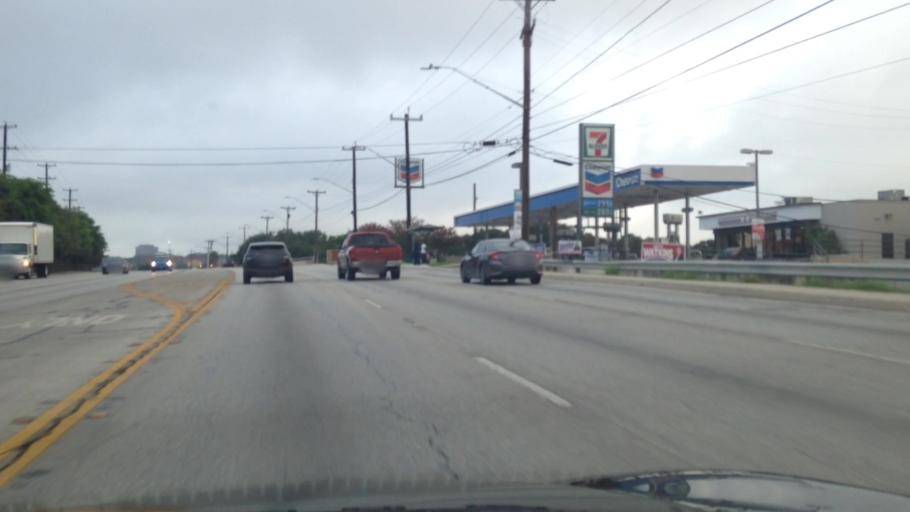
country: US
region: Texas
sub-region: Bexar County
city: Balcones Heights
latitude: 29.4976
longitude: -98.5562
